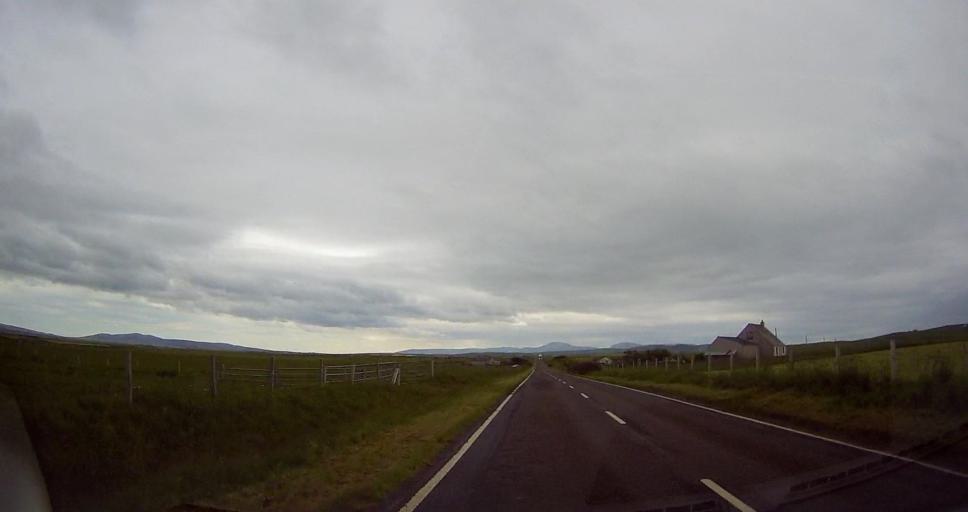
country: GB
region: Scotland
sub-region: Orkney Islands
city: Stromness
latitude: 59.0738
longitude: -3.2787
